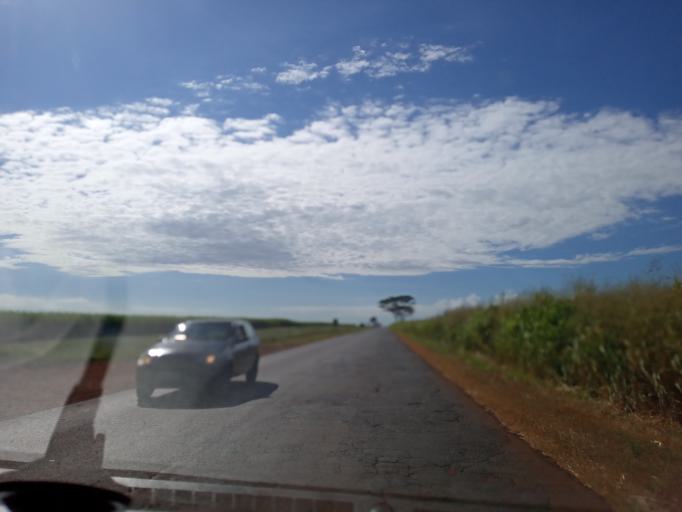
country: BR
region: Goias
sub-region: Itumbiara
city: Itumbiara
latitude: -18.4512
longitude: -49.1597
